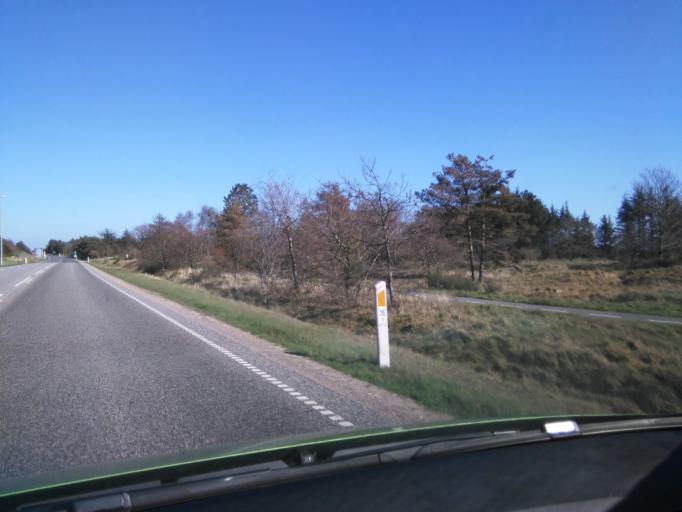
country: DK
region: South Denmark
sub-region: Varde Kommune
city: Oksbol
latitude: 55.6153
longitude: 8.2445
